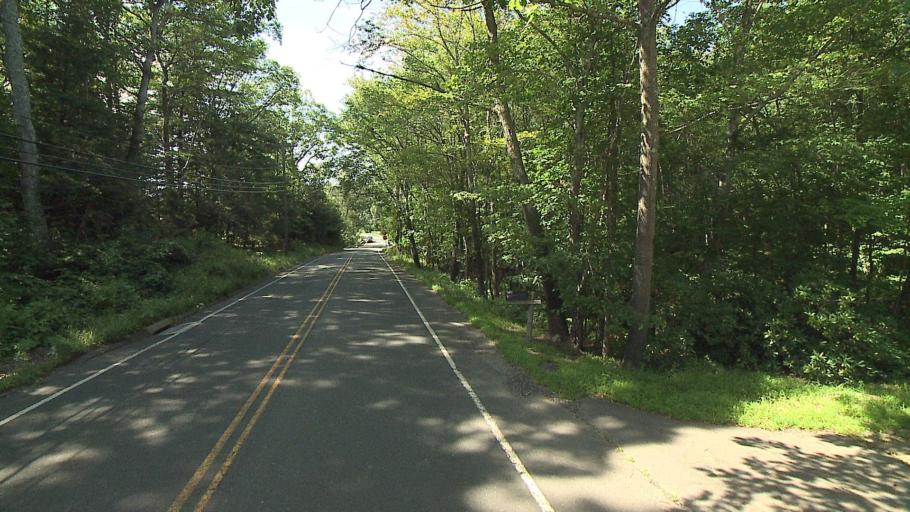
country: US
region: Connecticut
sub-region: Hartford County
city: West Simsbury
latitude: 41.8922
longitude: -72.8827
